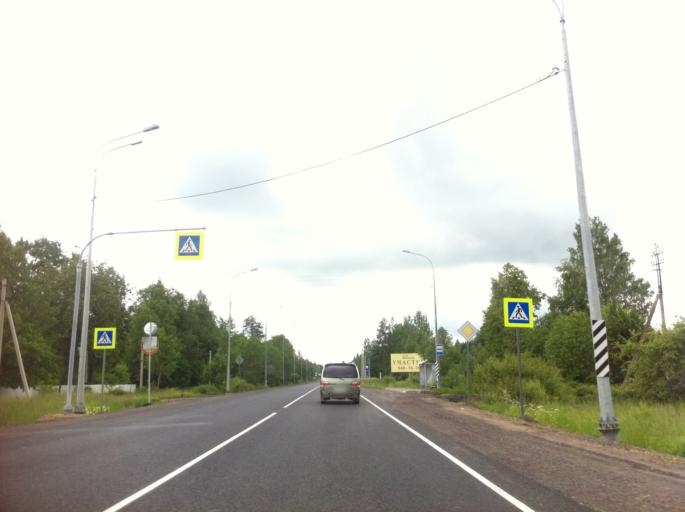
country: RU
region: Leningrad
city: Rozhdestveno
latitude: 59.1997
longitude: 29.9220
